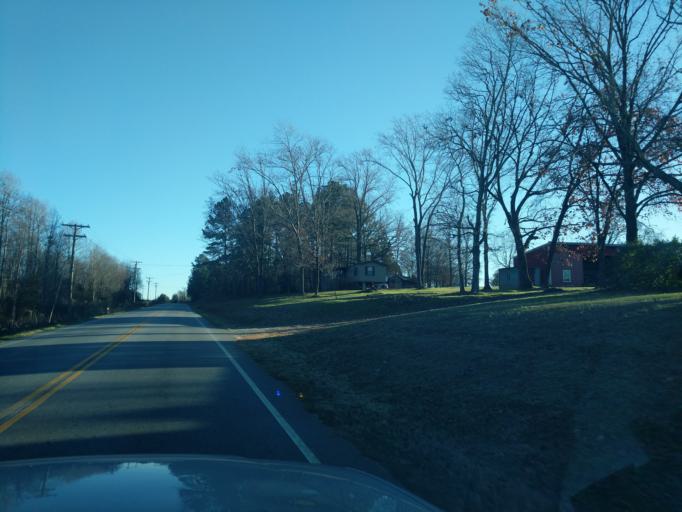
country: US
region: South Carolina
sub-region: Oconee County
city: Westminster
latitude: 34.6154
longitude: -83.0430
